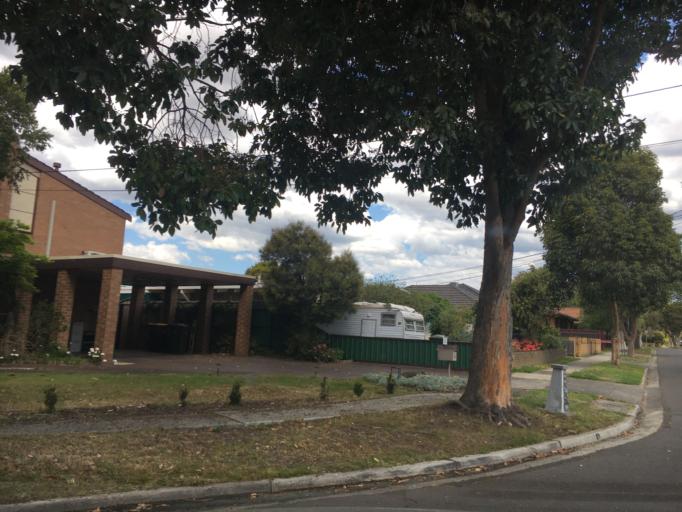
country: AU
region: Victoria
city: Hughesdale
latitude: -37.9068
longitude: 145.0923
